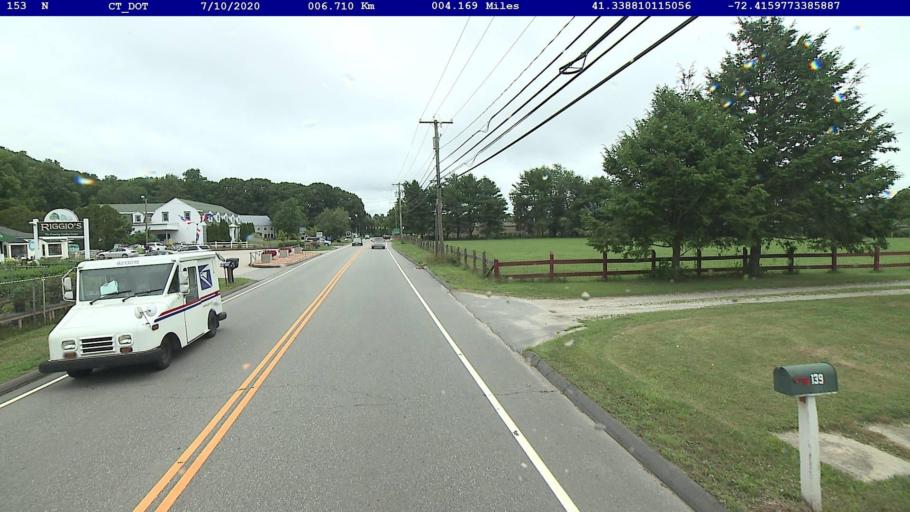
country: US
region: Connecticut
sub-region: Middlesex County
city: Essex Village
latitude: 41.3388
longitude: -72.4160
